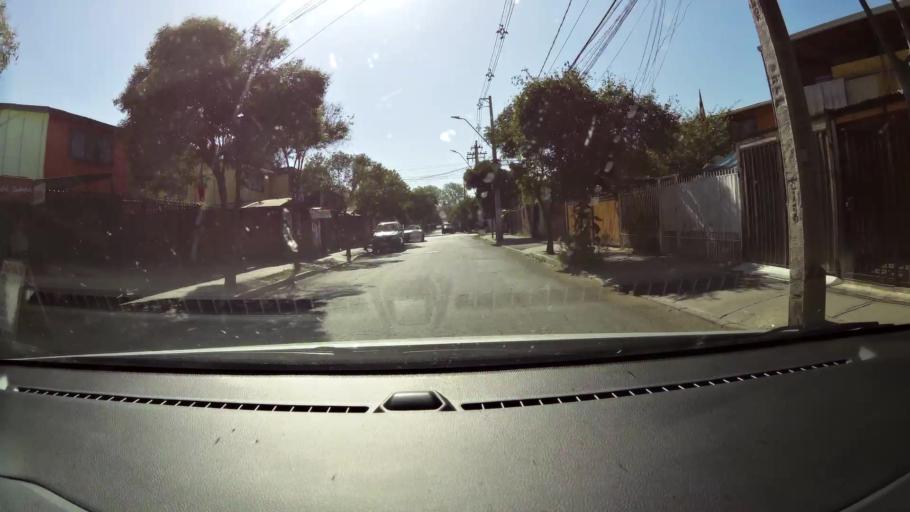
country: CL
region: Santiago Metropolitan
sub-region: Provincia de Maipo
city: San Bernardo
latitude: -33.5632
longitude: -70.7043
